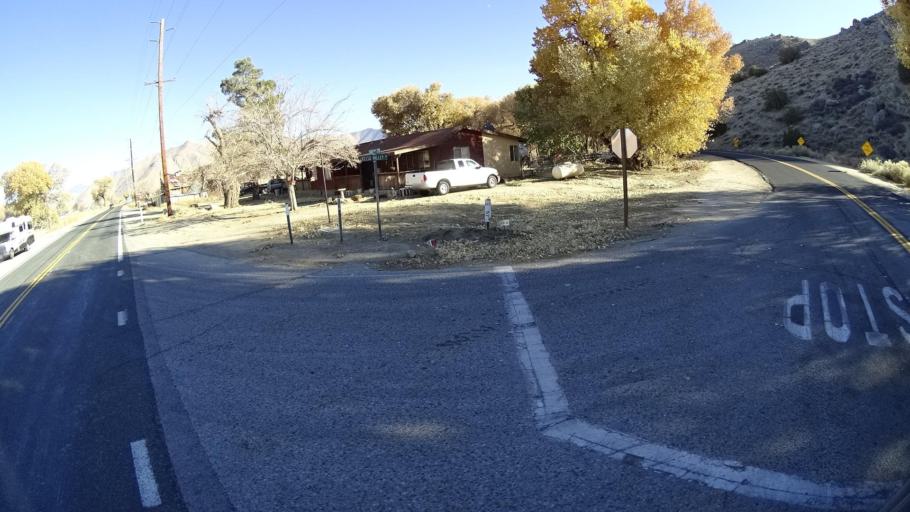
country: US
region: California
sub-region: Kern County
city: Weldon
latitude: 35.6642
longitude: -118.3032
